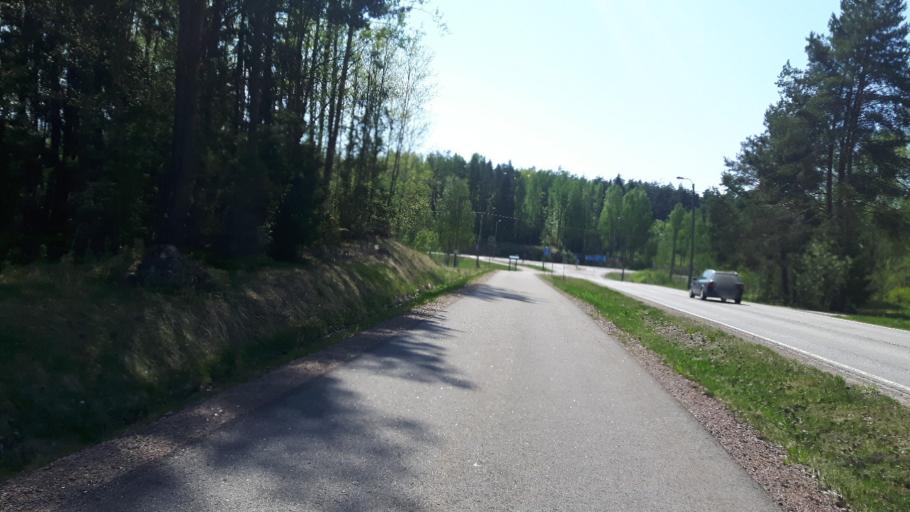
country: FI
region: Uusimaa
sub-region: Loviisa
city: Ruotsinpyhtaeae
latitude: 60.4970
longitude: 26.4424
